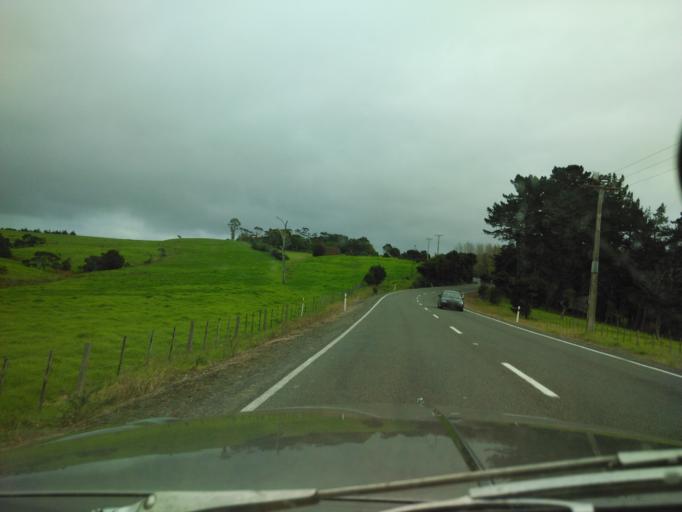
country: NZ
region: Auckland
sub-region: Auckland
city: Wellsford
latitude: -36.1305
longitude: 174.5628
